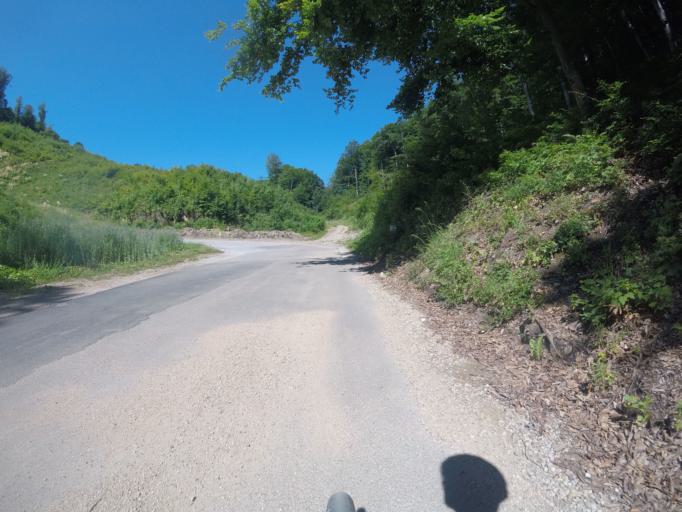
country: SI
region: Kostanjevica na Krki
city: Kostanjevica na Krki
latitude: 45.8155
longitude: 15.5104
